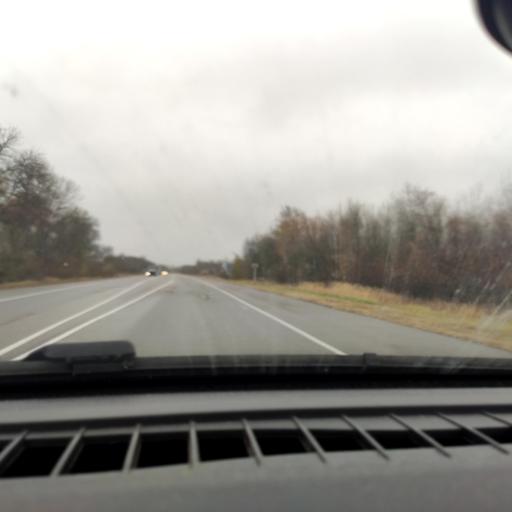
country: RU
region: Voronezj
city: Kolodeznyy
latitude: 51.3084
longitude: 39.0367
